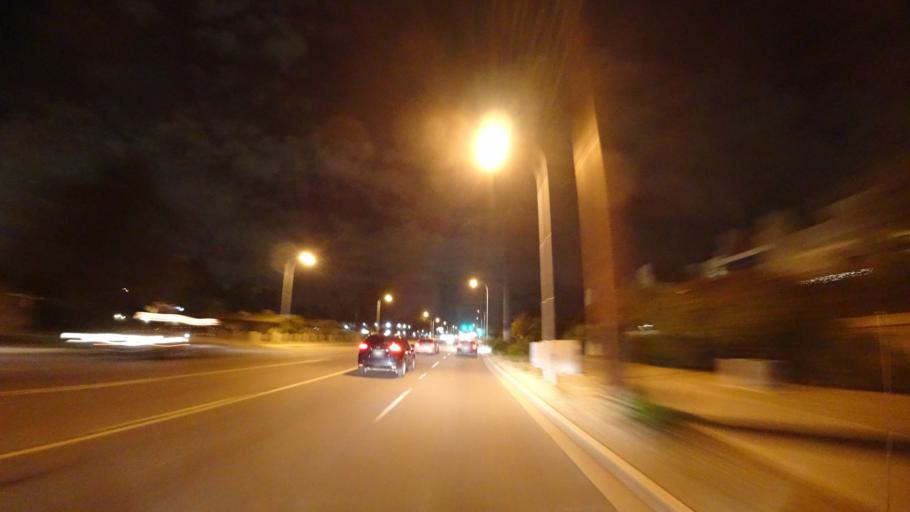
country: US
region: Arizona
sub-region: Maricopa County
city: Tempe
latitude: 33.4158
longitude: -111.9090
